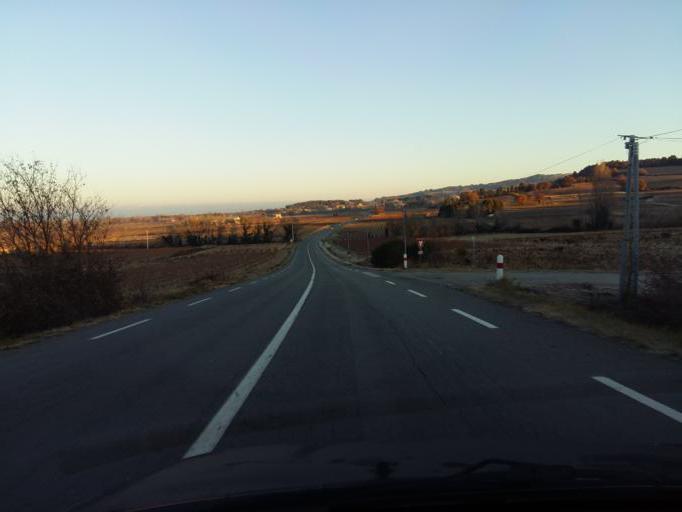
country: FR
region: Rhone-Alpes
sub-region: Departement de la Drome
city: Tulette
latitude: 44.2961
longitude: 4.9432
